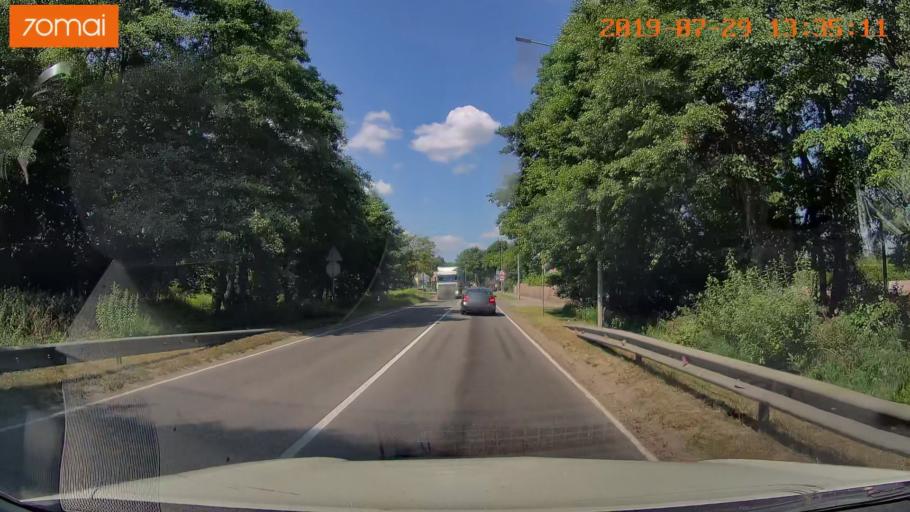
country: RU
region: Kaliningrad
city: Volochayevskoye
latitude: 54.6993
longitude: 20.2084
